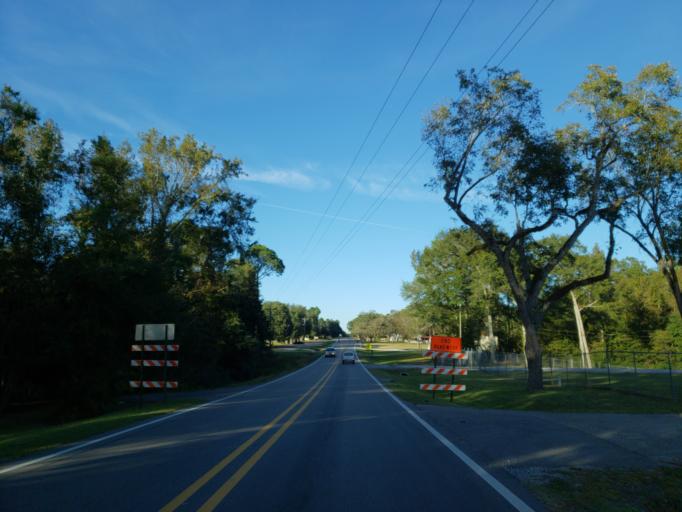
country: US
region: Mississippi
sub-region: Perry County
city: Richton
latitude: 31.3476
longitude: -88.7628
